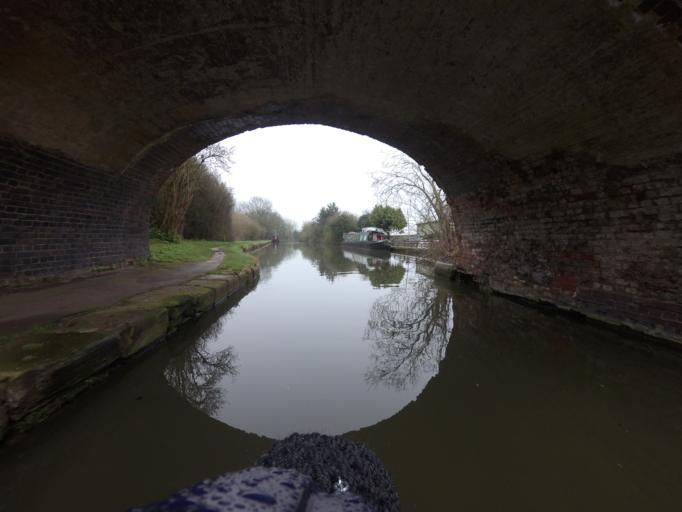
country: GB
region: England
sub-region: Milton Keynes
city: Simpson
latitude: 52.0096
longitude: -0.7163
